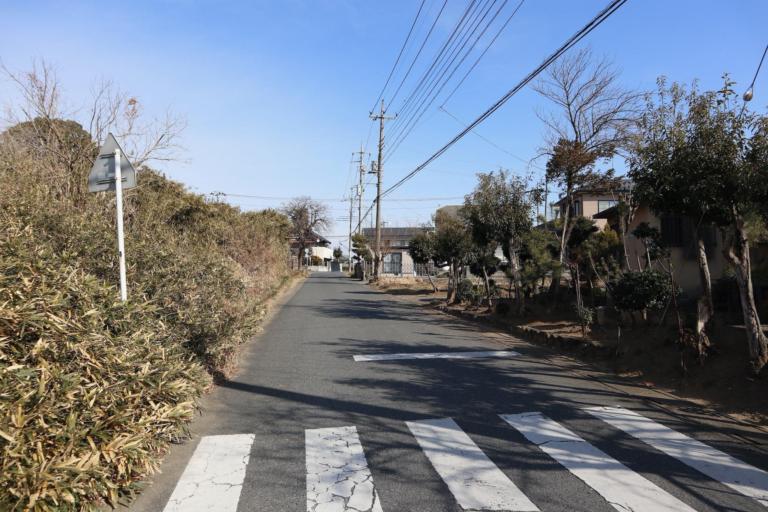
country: JP
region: Saitama
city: Fukiage-fujimi
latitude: 36.0712
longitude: 139.4226
